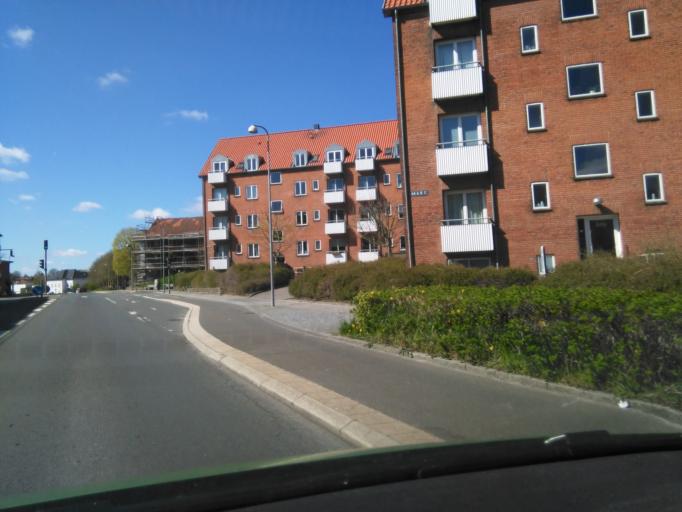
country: DK
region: Central Jutland
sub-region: Horsens Kommune
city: Horsens
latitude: 55.8552
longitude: 9.8347
